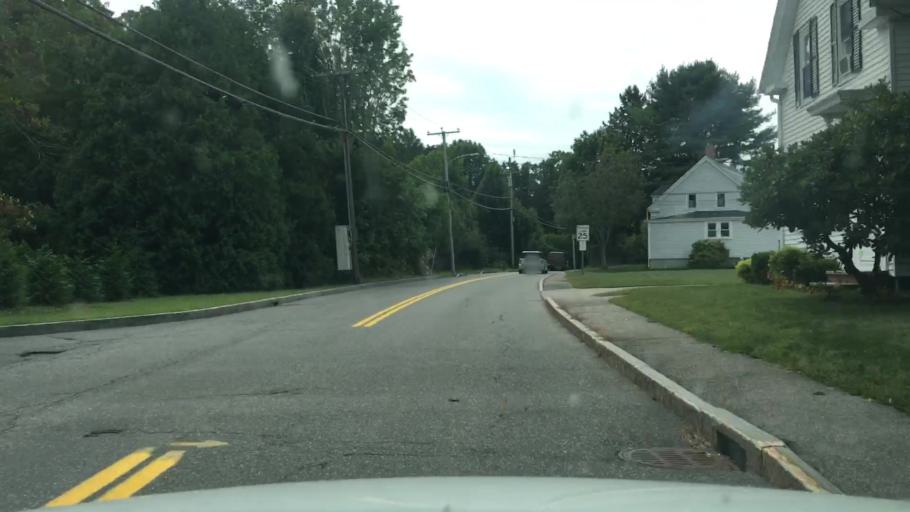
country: US
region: Maine
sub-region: York County
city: Kittery
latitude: 43.0919
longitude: -70.7384
